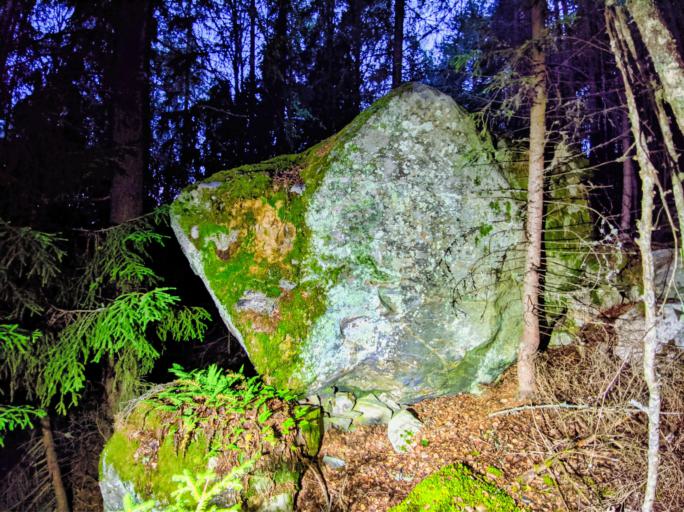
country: NO
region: Buskerud
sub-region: Gol
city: Gol
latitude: 60.7060
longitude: 8.9572
